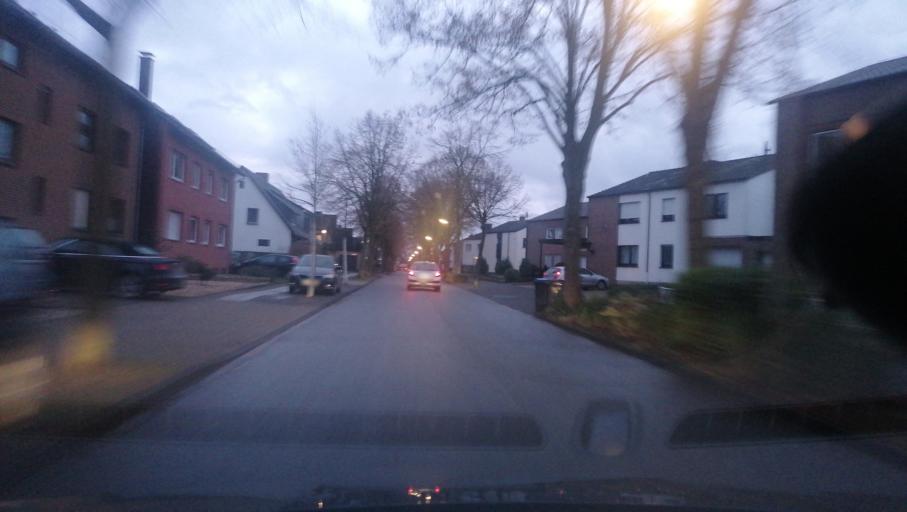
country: DE
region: North Rhine-Westphalia
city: Oer-Erkenschwick
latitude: 51.6301
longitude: 7.2909
